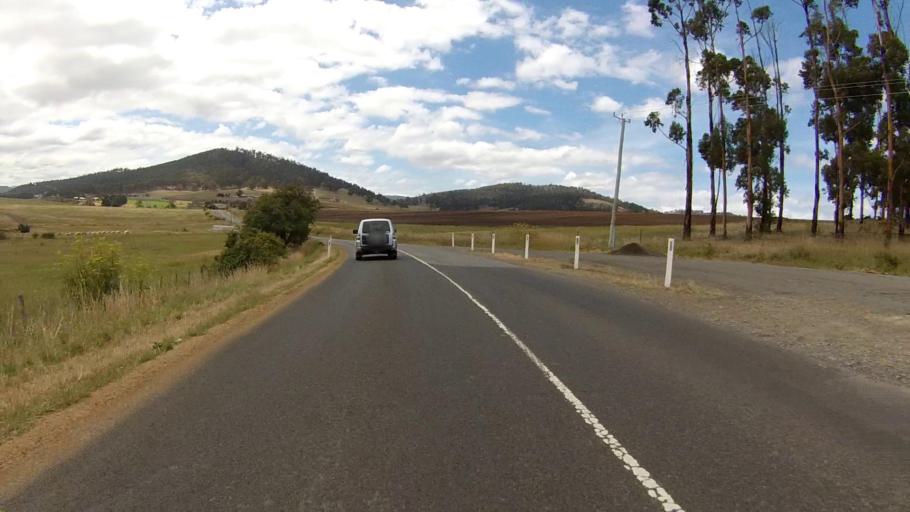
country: AU
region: Tasmania
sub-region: Sorell
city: Sorell
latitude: -42.8077
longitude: 147.6125
